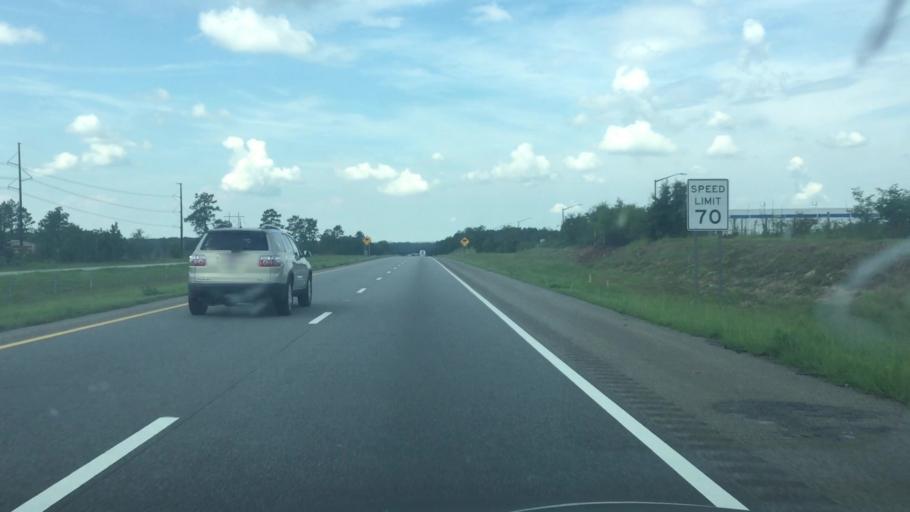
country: US
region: North Carolina
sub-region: Richmond County
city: Hamlet
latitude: 34.8545
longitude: -79.7102
